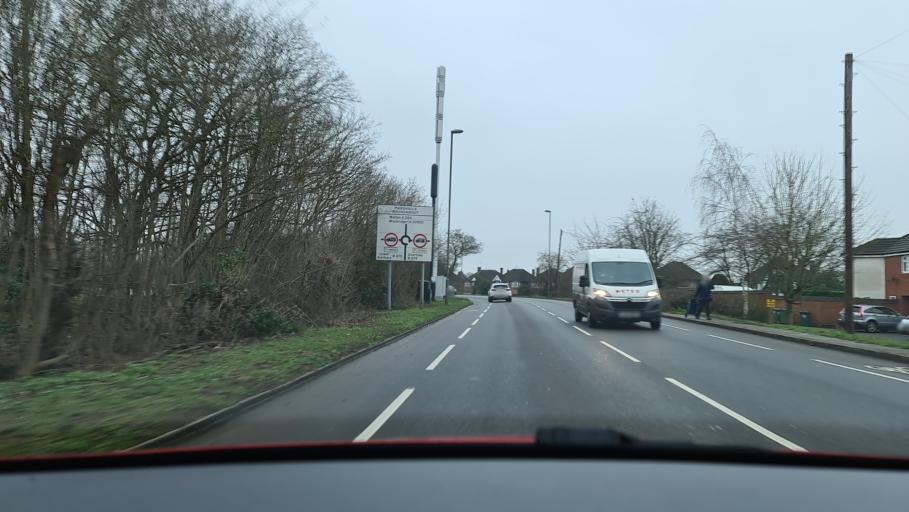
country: GB
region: England
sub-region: Surrey
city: Shepperton
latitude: 51.3948
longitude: -0.4357
